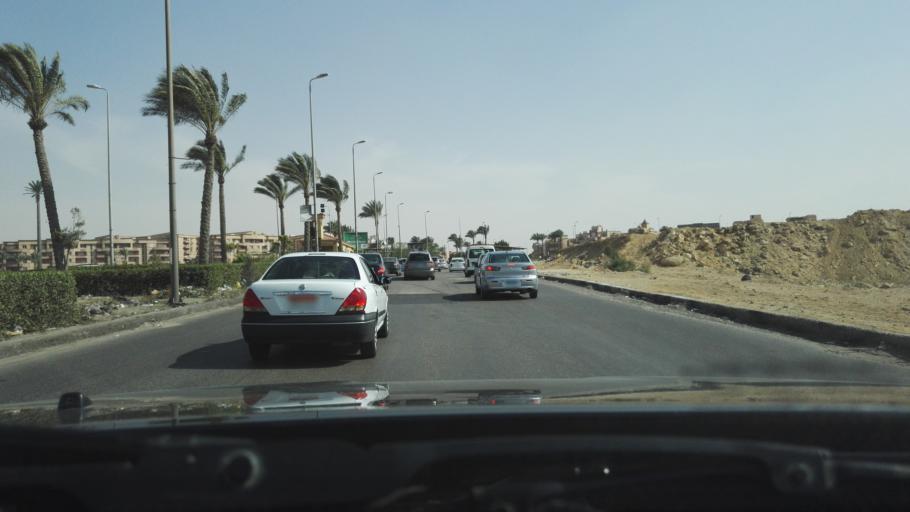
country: EG
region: Muhafazat al Qalyubiyah
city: Al Khankah
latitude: 30.0731
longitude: 31.4732
